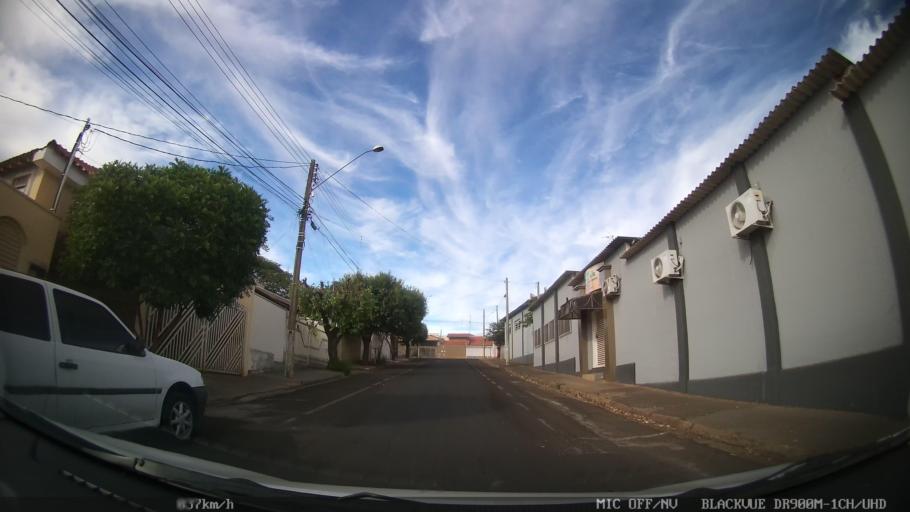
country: BR
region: Sao Paulo
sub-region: Catanduva
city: Catanduva
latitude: -21.1371
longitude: -48.9934
